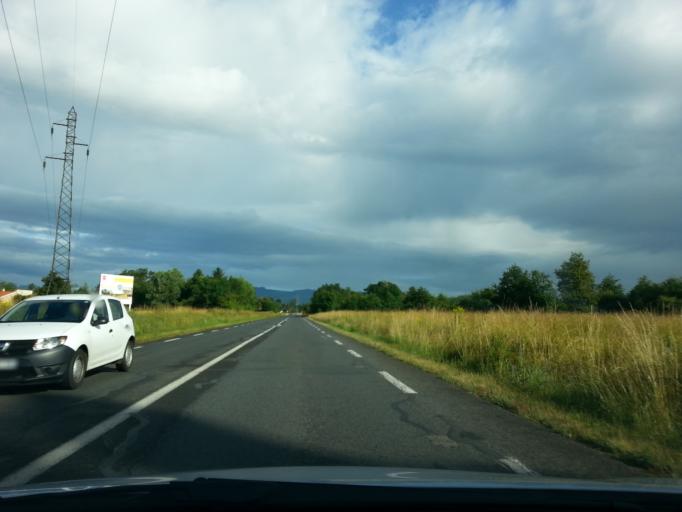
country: FR
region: Rhone-Alpes
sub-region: Departement du Rhone
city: Belleville
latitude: 46.1151
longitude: 4.7509
